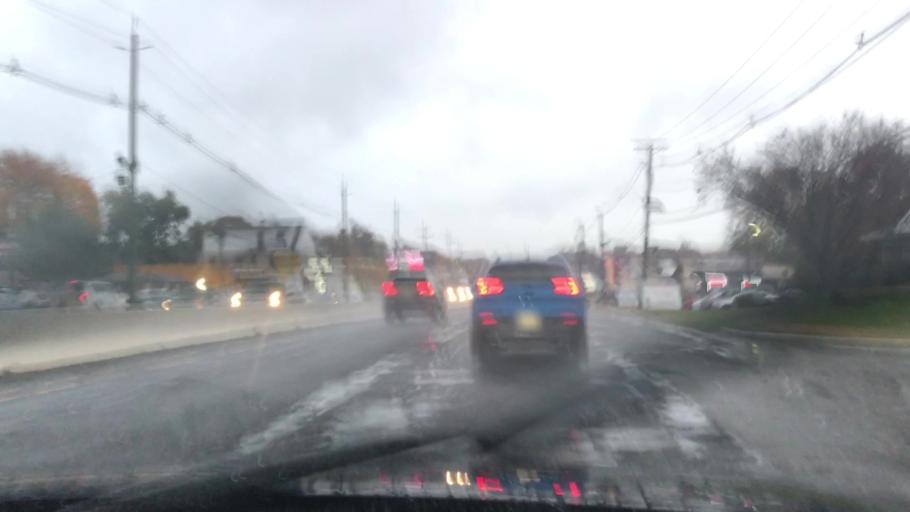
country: US
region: New Jersey
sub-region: Bergen County
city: Lodi
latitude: 40.8766
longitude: -74.0730
